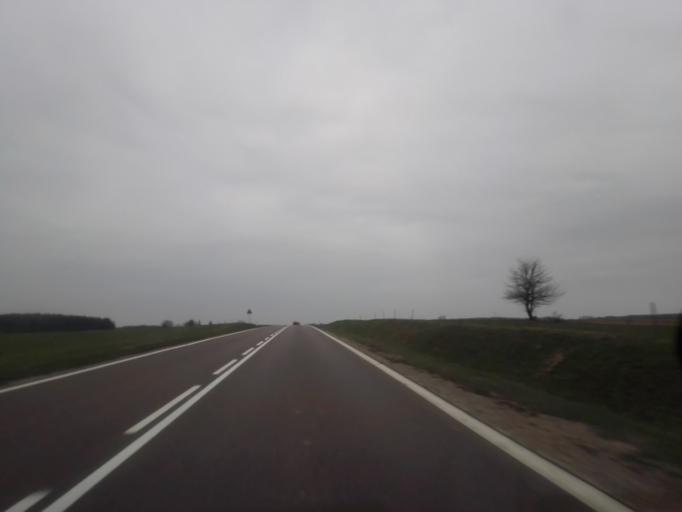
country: PL
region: Podlasie
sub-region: Powiat grajewski
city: Szczuczyn
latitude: 53.5102
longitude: 22.2415
